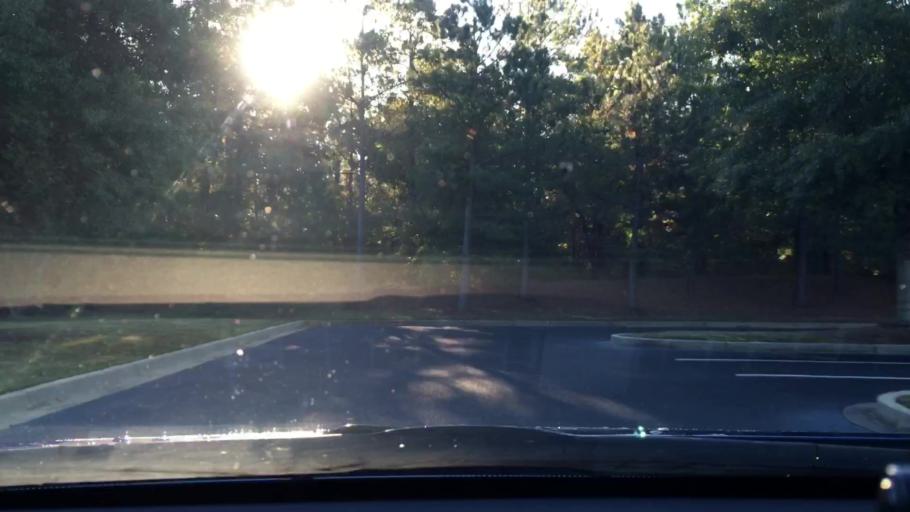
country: US
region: South Carolina
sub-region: Lexington County
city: Irmo
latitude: 34.0846
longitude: -81.1513
